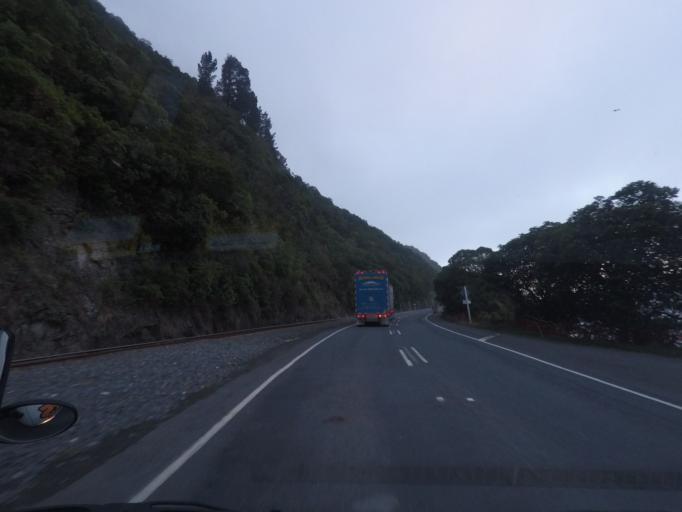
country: NZ
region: Canterbury
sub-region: Kaikoura District
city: Kaikoura
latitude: -42.4506
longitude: 173.5696
